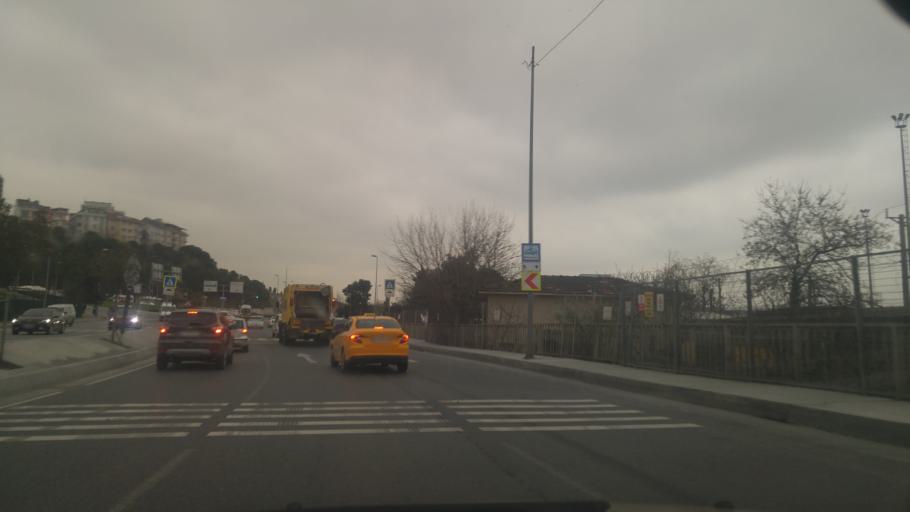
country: TR
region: Istanbul
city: Mahmutbey
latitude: 41.0212
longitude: 28.7673
